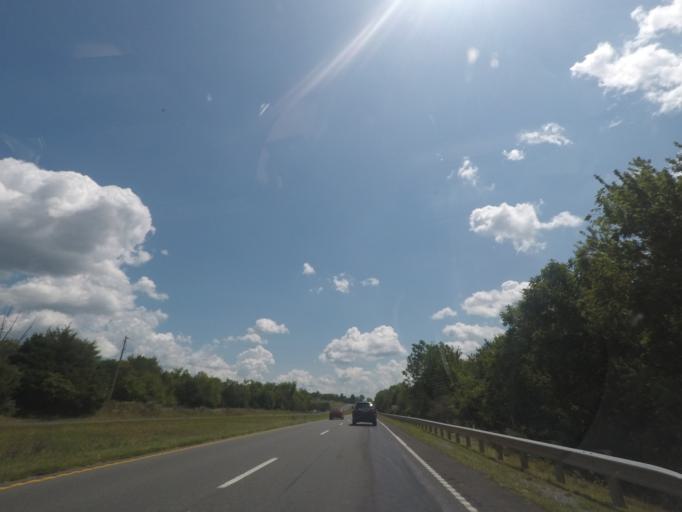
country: US
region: Virginia
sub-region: City of Winchester
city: Winchester
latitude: 39.0961
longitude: -78.1064
